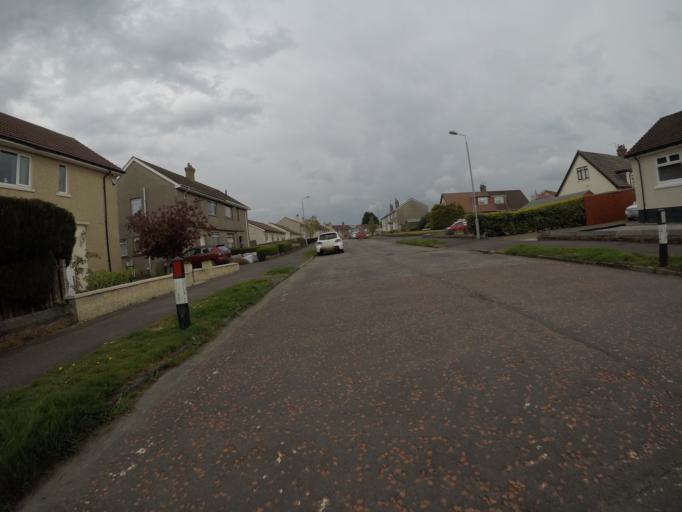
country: GB
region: Scotland
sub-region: East Ayrshire
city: Kilmaurs
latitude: 55.6420
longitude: -4.5315
